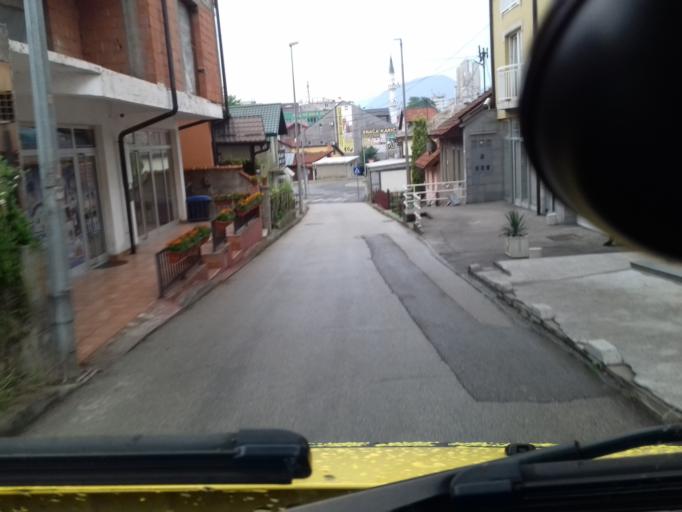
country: BA
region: Federation of Bosnia and Herzegovina
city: Zenica
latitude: 44.1976
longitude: 17.9081
